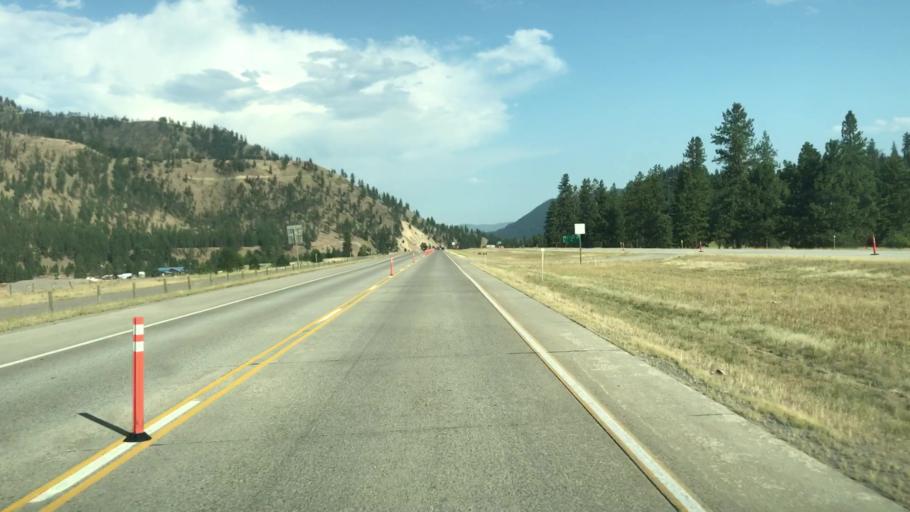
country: US
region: Montana
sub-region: Mineral County
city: Superior
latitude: 47.2301
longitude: -114.9778
